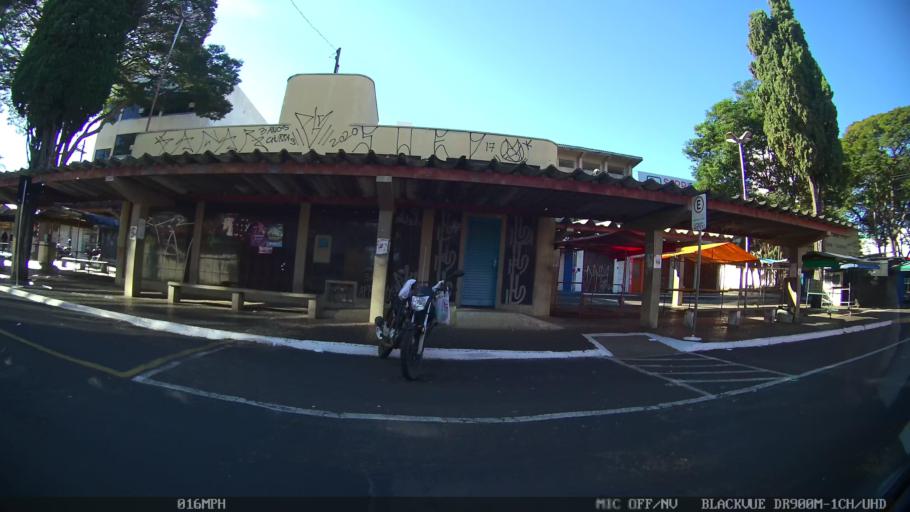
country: BR
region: Sao Paulo
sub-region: Franca
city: Franca
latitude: -20.5372
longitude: -47.4028
